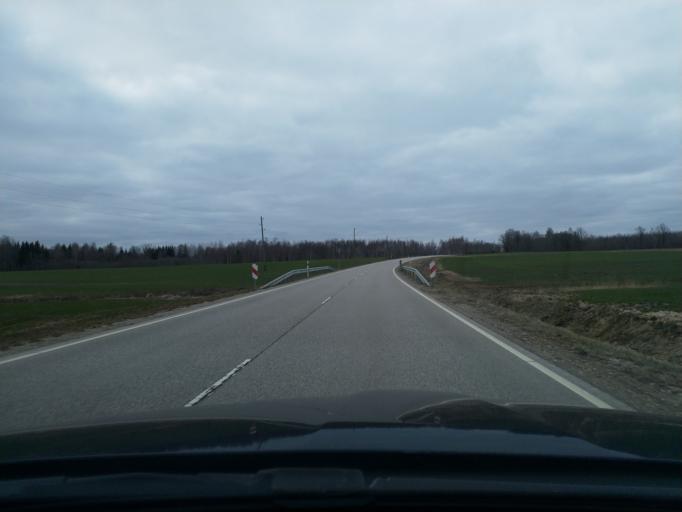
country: LV
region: Talsu Rajons
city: Sabile
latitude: 56.9438
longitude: 22.4847
